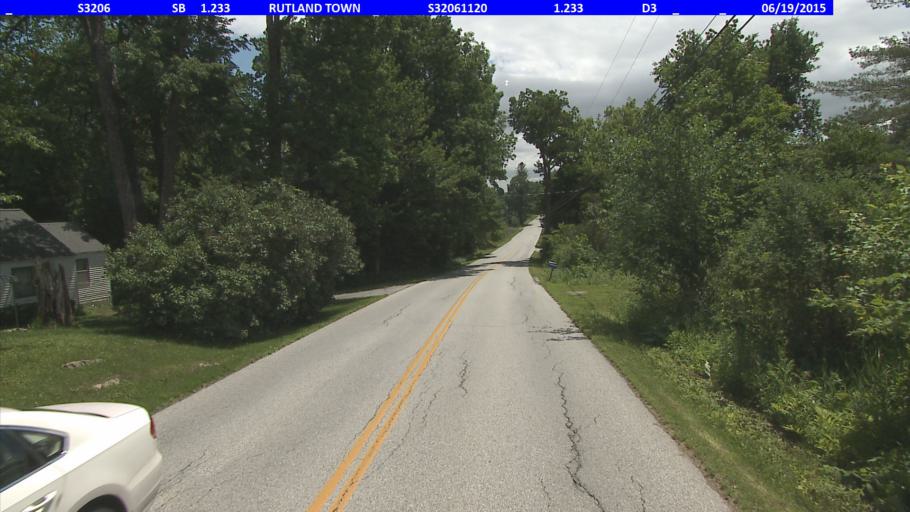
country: US
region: Vermont
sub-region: Rutland County
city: Rutland
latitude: 43.6465
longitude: -72.9954
